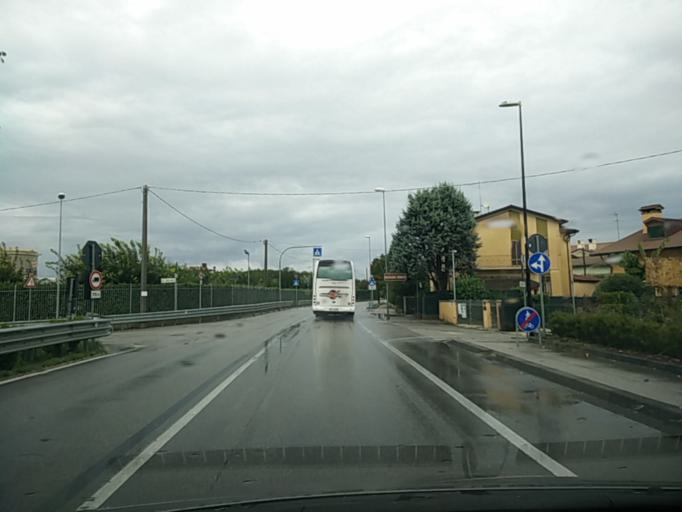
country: IT
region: Veneto
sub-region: Provincia di Vicenza
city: Rossano Veneto
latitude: 45.7013
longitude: 11.8207
